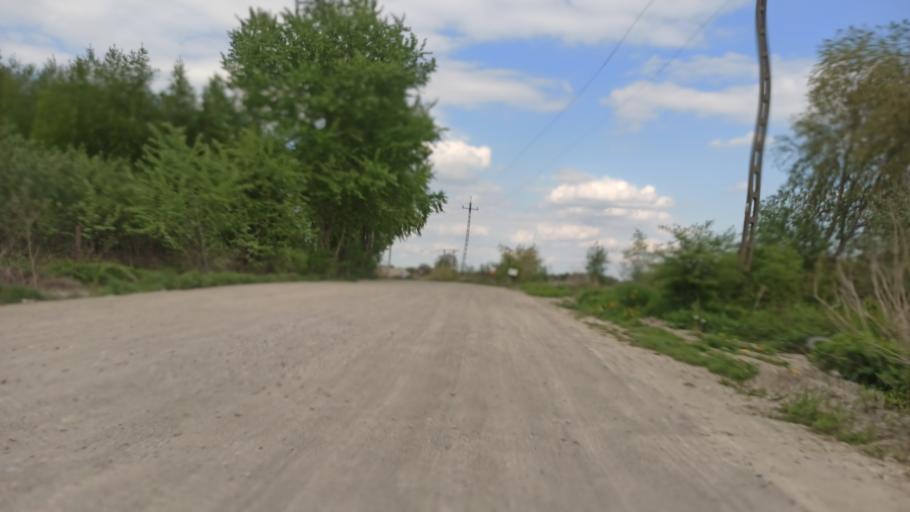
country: PL
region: Subcarpathian Voivodeship
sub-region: Powiat jaroslawski
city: Radymno
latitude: 49.9572
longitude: 22.8255
